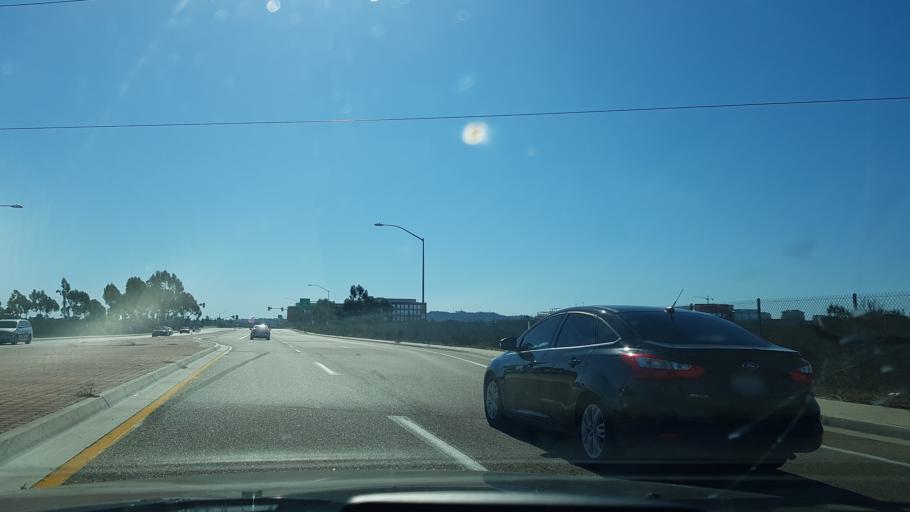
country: US
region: California
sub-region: San Diego County
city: La Jolla
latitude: 32.8723
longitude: -117.1925
